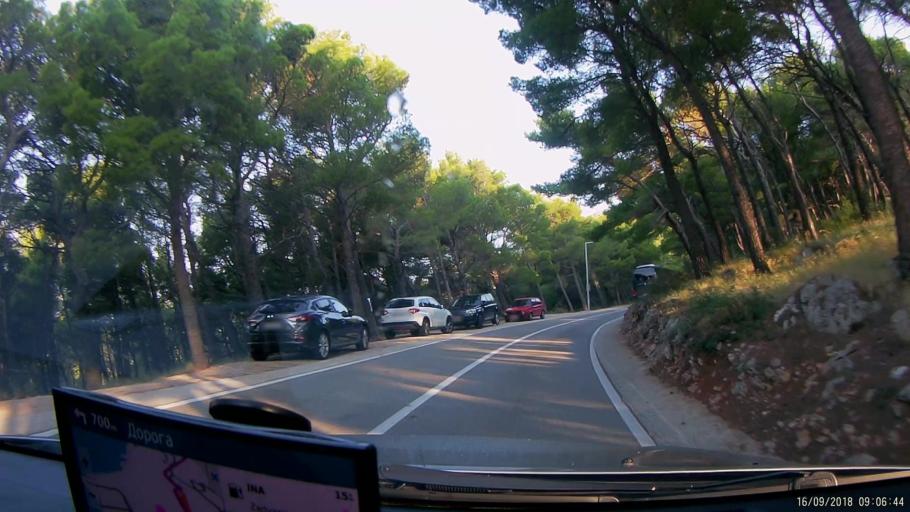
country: HR
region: Splitsko-Dalmatinska
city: Donja Brela
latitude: 43.3707
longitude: 16.9281
